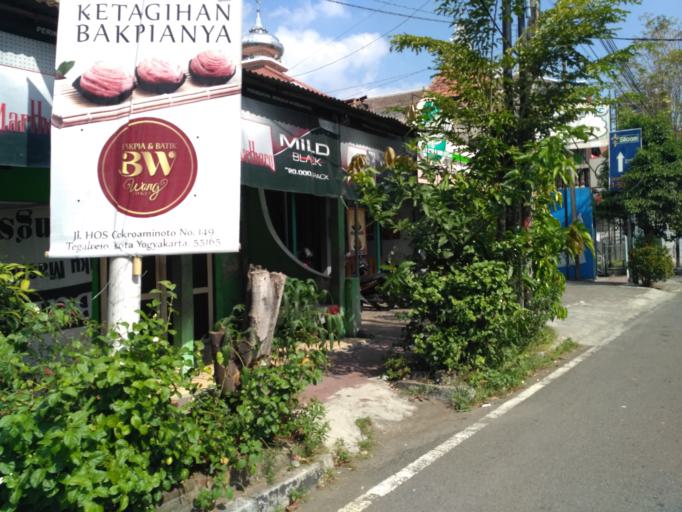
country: ID
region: Daerah Istimewa Yogyakarta
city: Depok
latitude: -7.7594
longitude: 110.3954
